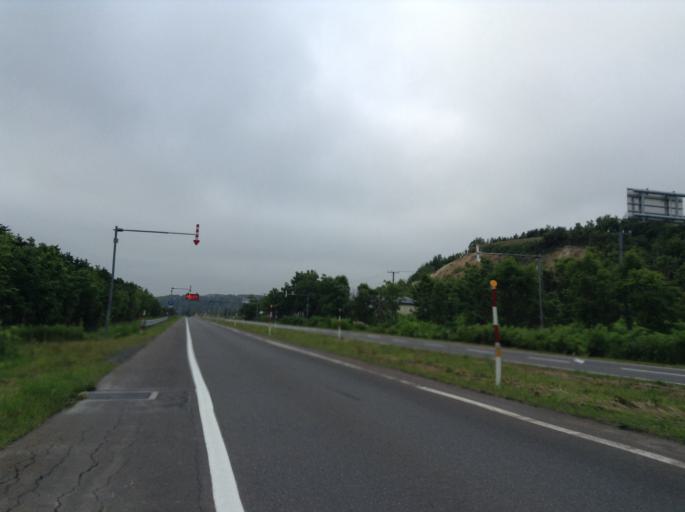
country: JP
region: Hokkaido
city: Wakkanai
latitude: 45.3668
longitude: 141.7281
